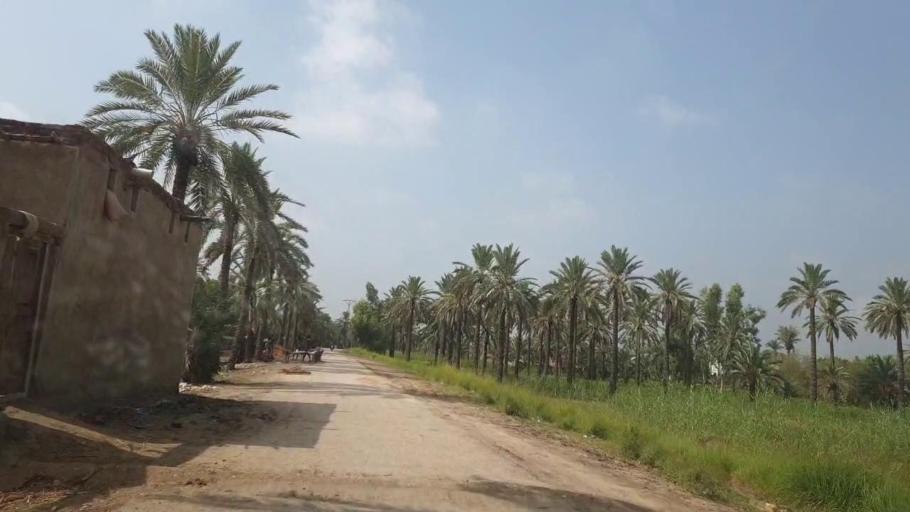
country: PK
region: Sindh
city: Khairpur
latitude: 27.5596
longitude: 68.7593
